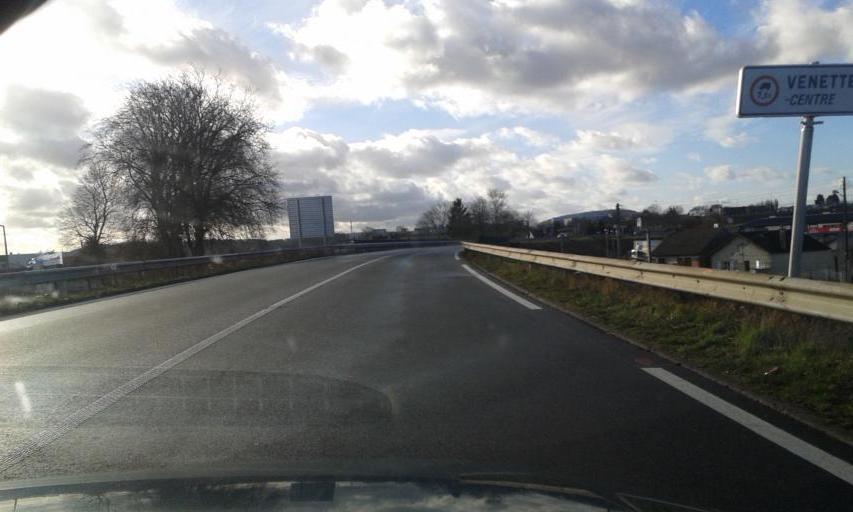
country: FR
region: Picardie
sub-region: Departement de l'Oise
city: Venette
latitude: 49.4092
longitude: 2.7957
